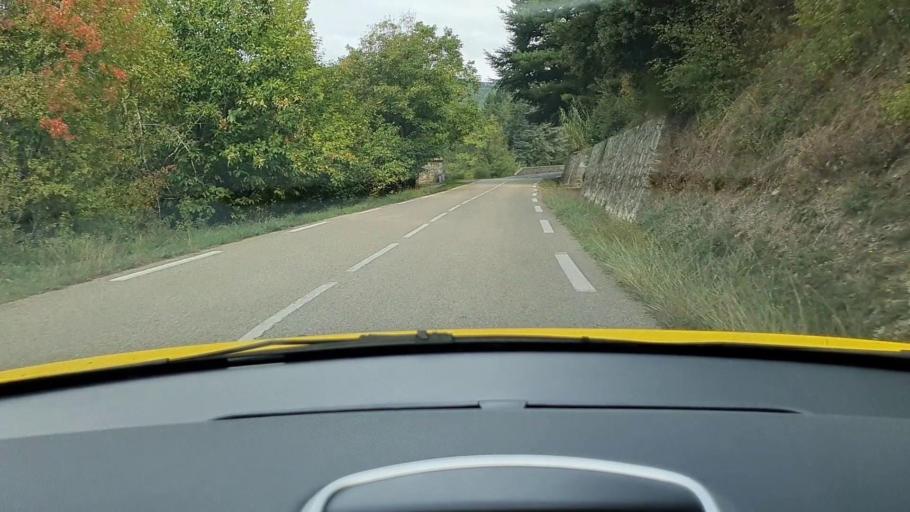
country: FR
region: Languedoc-Roussillon
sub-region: Departement du Gard
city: Le Vigan
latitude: 43.9957
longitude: 3.5898
